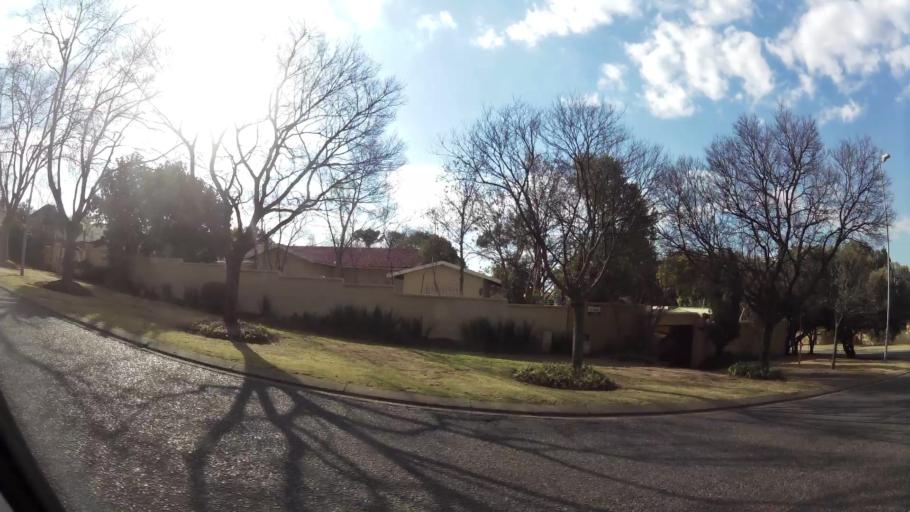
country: ZA
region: Gauteng
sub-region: City of Johannesburg Metropolitan Municipality
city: Diepsloot
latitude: -26.0075
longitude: 28.0281
